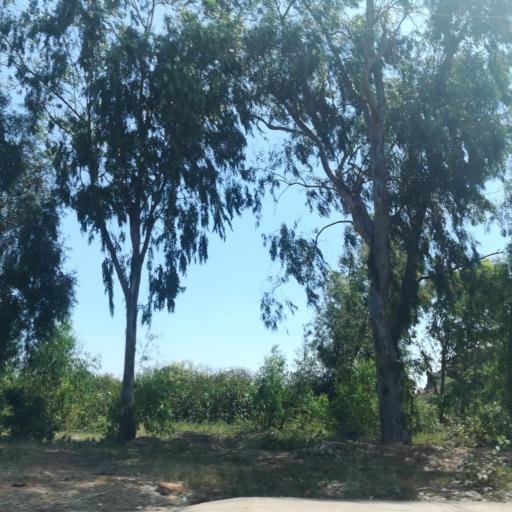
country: NG
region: Plateau
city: Bukuru
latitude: 9.8096
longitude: 8.8716
